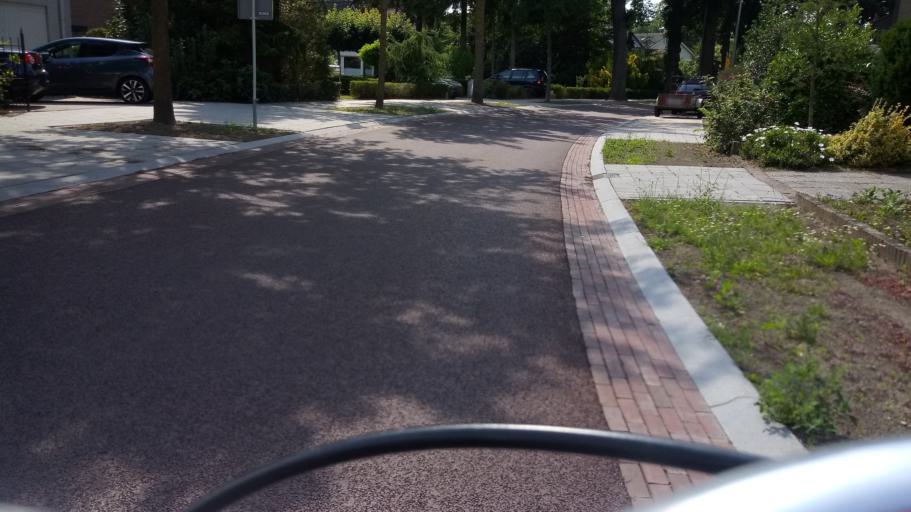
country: NL
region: Gelderland
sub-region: Gemeente Nijmegen
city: Nijmegen
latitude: 51.8396
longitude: 5.8278
